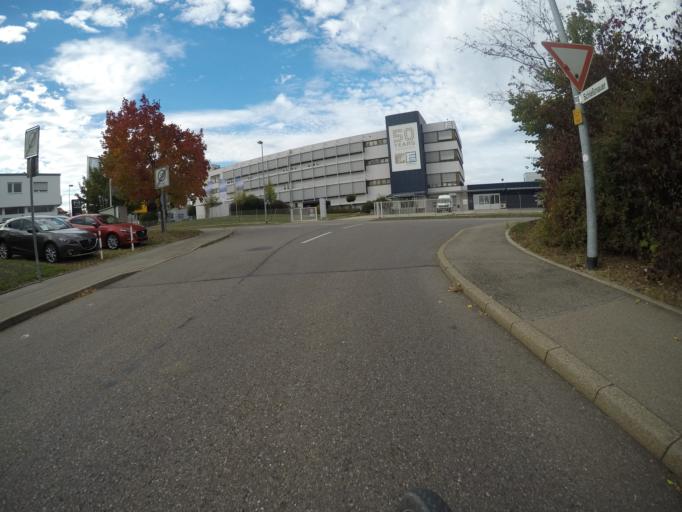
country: DE
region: Baden-Wuerttemberg
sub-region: Regierungsbezirk Stuttgart
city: Herrenberg
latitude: 48.5996
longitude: 8.8625
